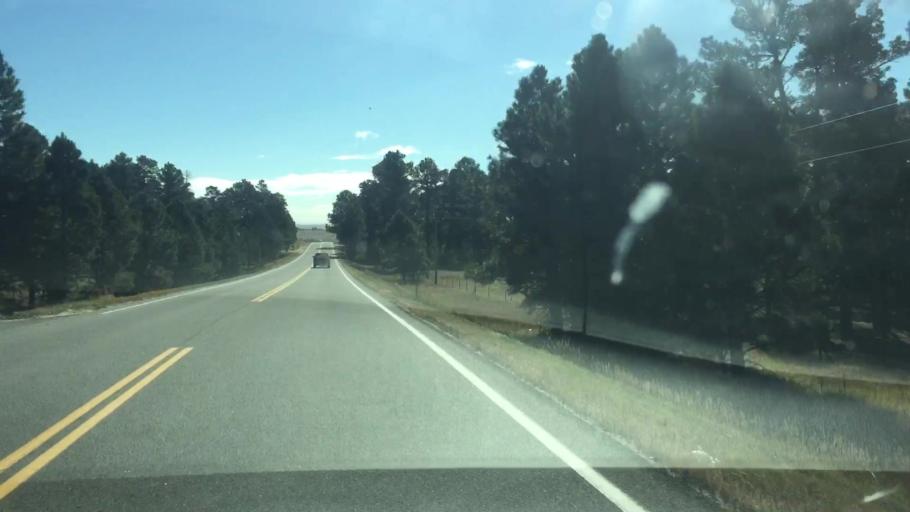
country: US
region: Colorado
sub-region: Elbert County
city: Kiowa
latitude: 39.3310
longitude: -104.4104
